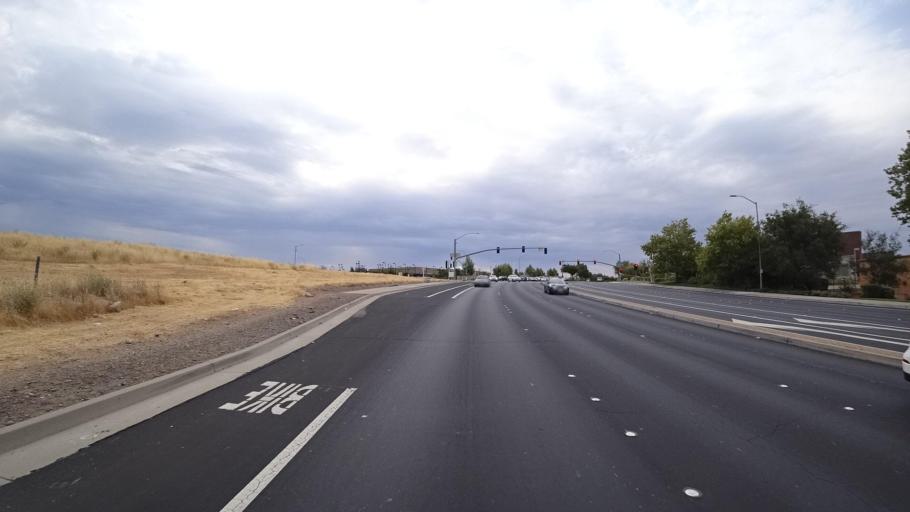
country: US
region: California
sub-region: Placer County
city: Rocklin
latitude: 38.7621
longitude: -121.2487
